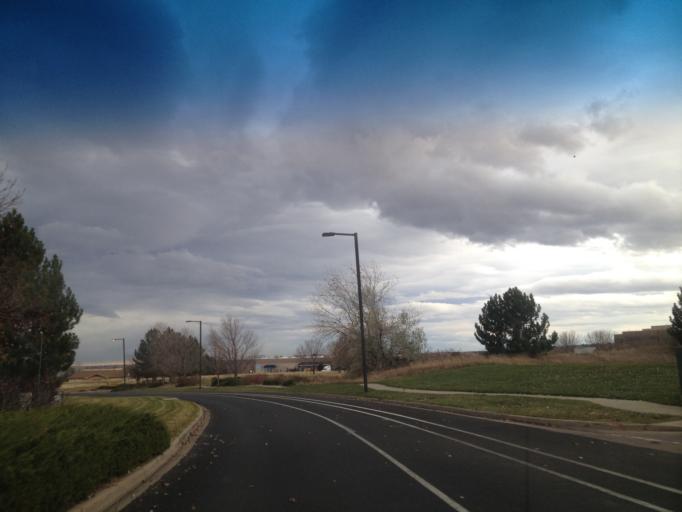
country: US
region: Colorado
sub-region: Boulder County
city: Superior
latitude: 39.9659
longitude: -105.1705
